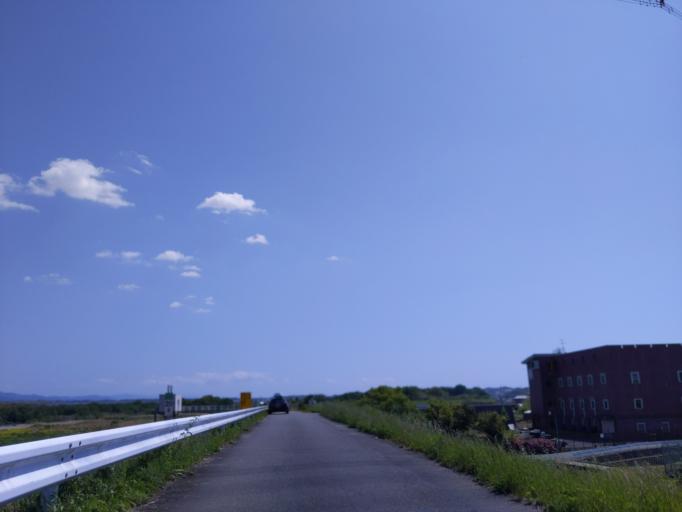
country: JP
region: Kyoto
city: Tanabe
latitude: 34.7590
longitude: 135.8032
